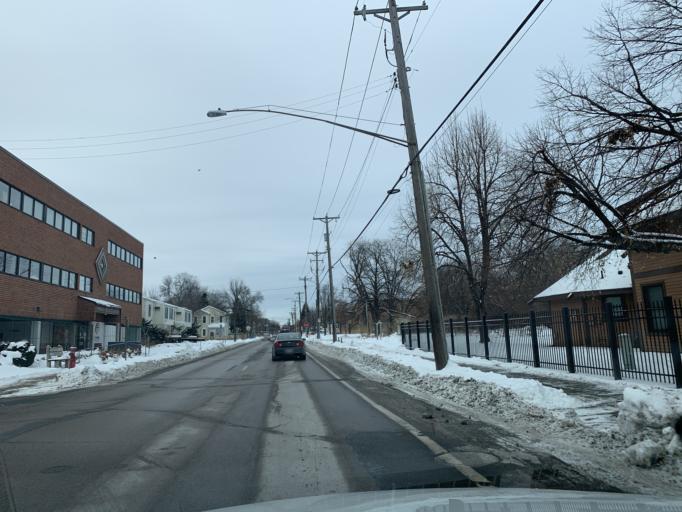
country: US
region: Minnesota
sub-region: Hennepin County
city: Minneapolis
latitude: 44.9592
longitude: -93.2548
